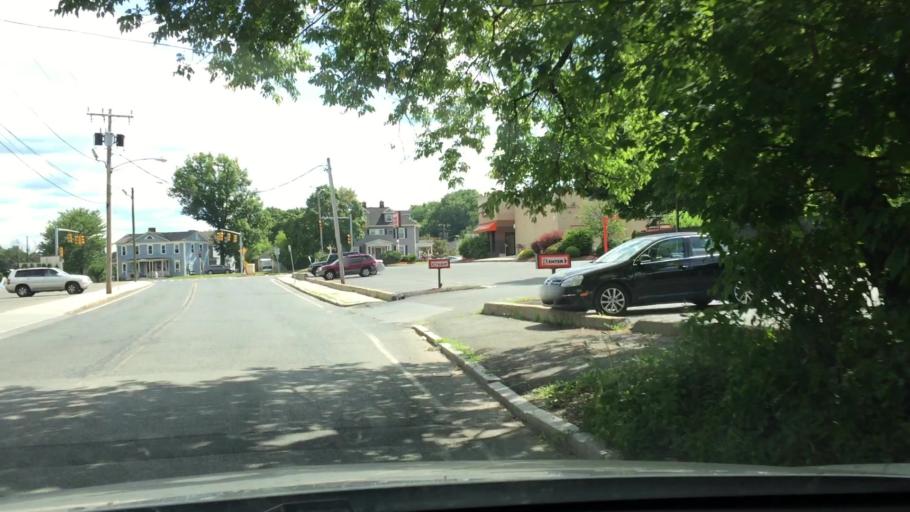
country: US
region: Massachusetts
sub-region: Berkshire County
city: Pittsfield
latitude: 42.4481
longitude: -73.2450
